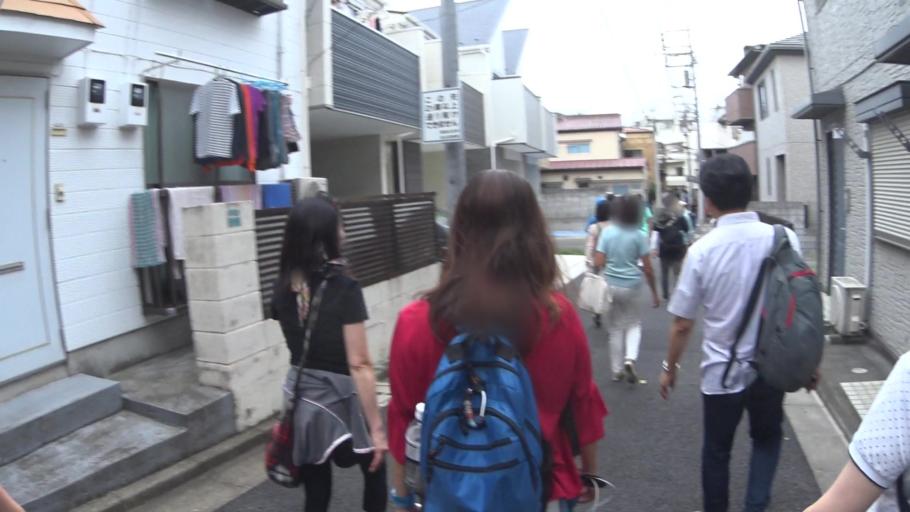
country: JP
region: Tokyo
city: Tokyo
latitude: 35.7197
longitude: 139.7170
